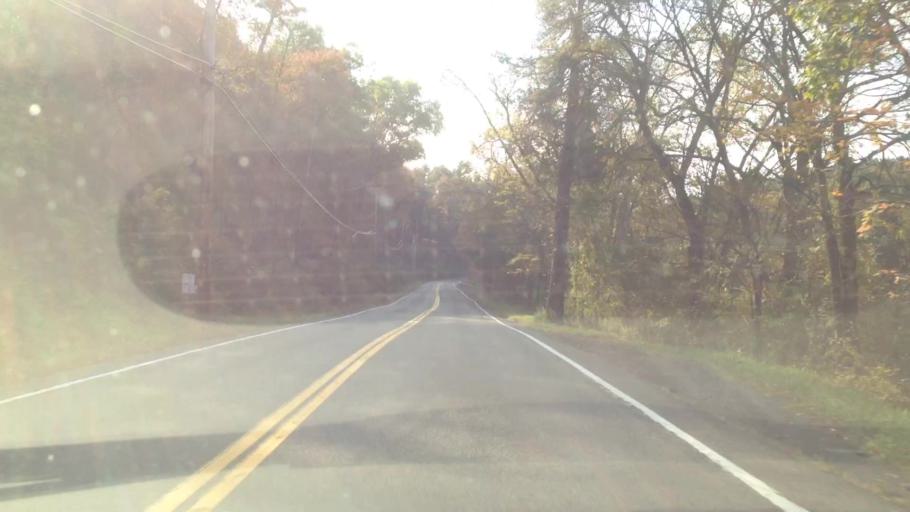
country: US
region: New York
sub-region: Ulster County
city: Tillson
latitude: 41.8258
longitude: -74.0464
